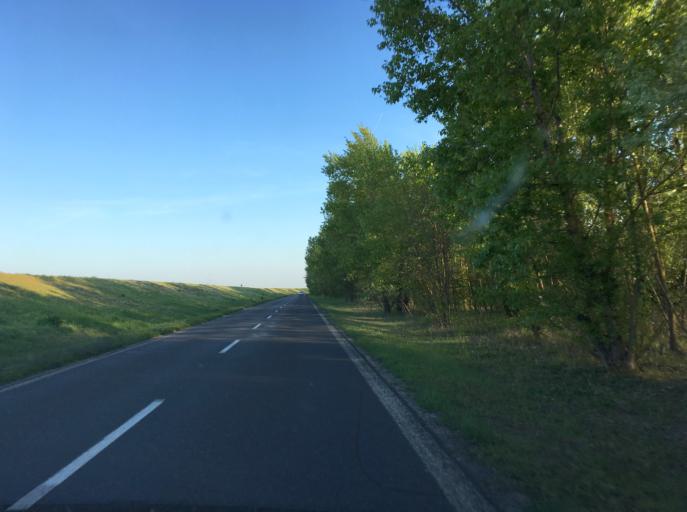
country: HU
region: Gyor-Moson-Sopron
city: Rajka
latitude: 48.0224
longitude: 17.2470
